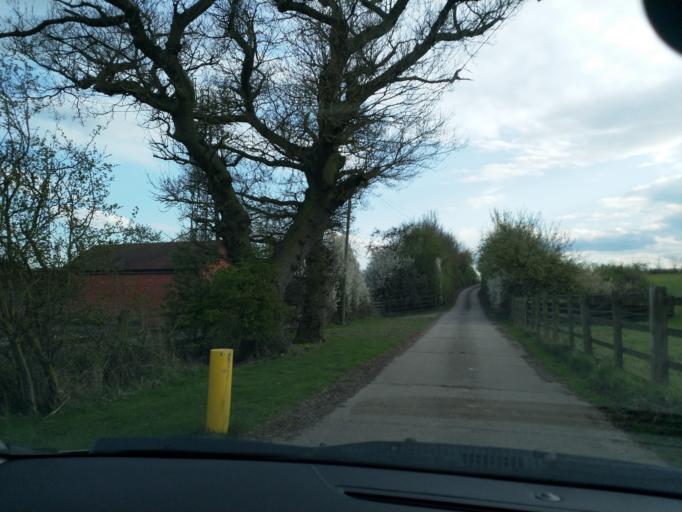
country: GB
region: England
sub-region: Warwickshire
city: Royal Leamington Spa
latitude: 52.2328
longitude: -1.5330
